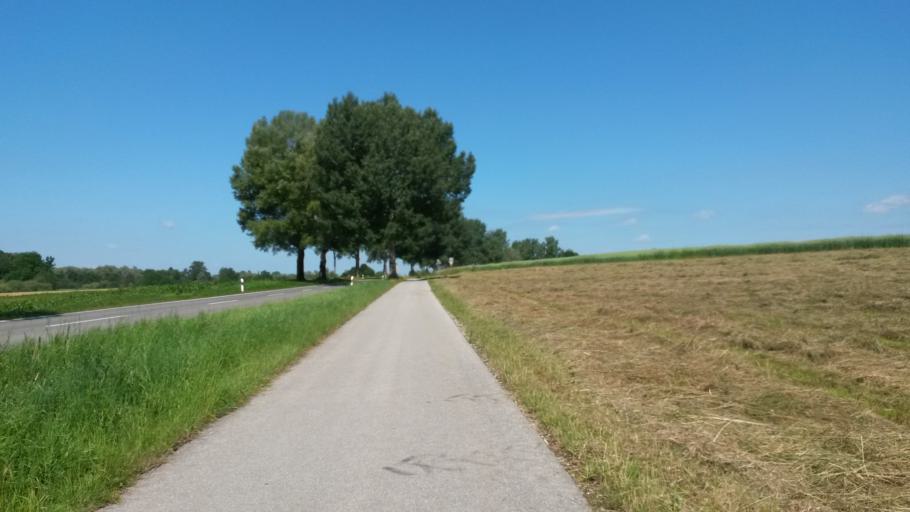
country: DE
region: Bavaria
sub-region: Upper Bavaria
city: Grabenstatt
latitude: 47.8565
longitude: 12.5343
